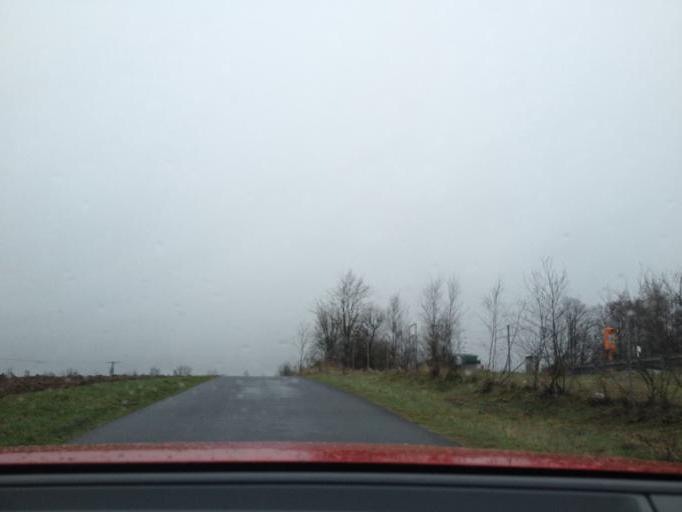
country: DE
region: Bavaria
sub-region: Upper Franconia
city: Thierstein
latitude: 50.0881
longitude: 12.1020
